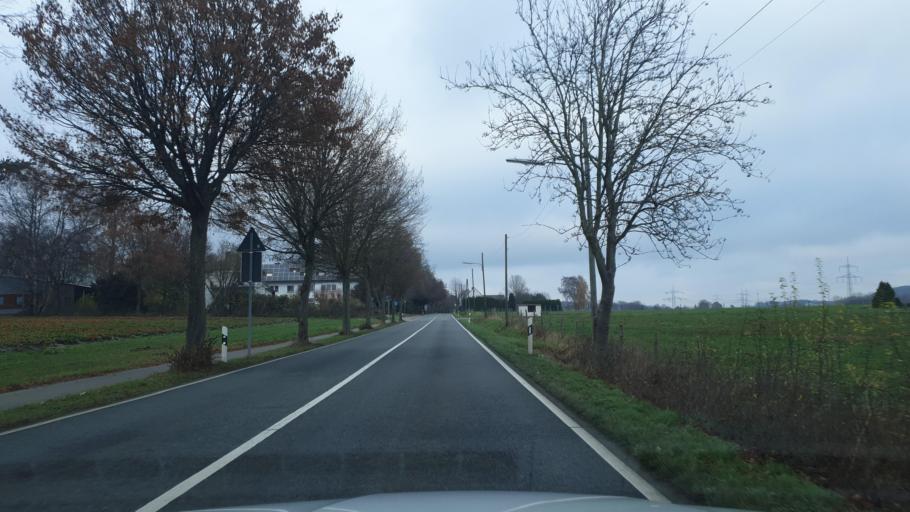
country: DE
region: North Rhine-Westphalia
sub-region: Regierungsbezirk Detmold
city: Hiddenhausen
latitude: 52.1499
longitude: 8.6215
